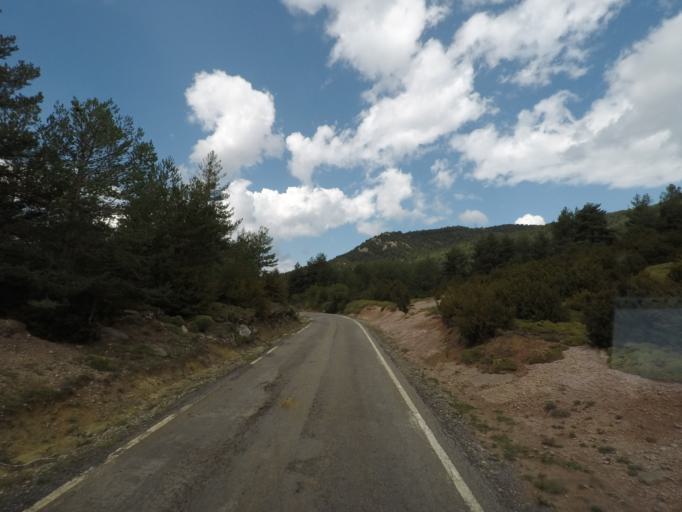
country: ES
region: Aragon
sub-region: Provincia de Huesca
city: Fiscal
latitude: 42.4028
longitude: -0.0567
